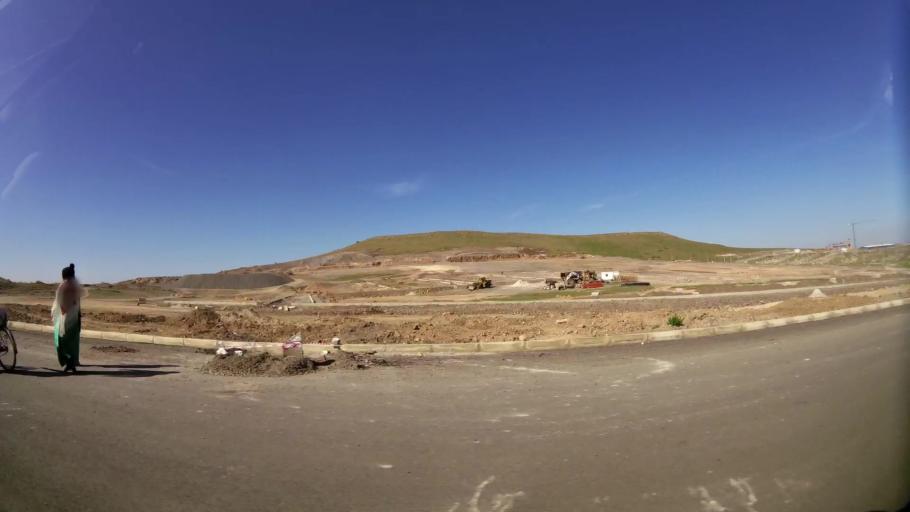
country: MA
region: Oriental
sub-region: Oujda-Angad
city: Oujda
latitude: 34.6483
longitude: -1.9523
